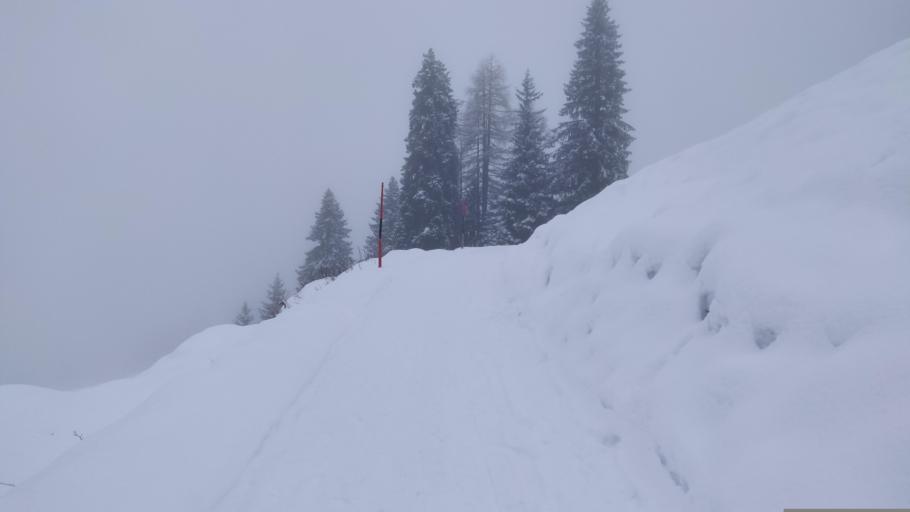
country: CH
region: Bern
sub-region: Interlaken-Oberhasli District
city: Lauterbrunnen
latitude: 46.5907
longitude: 7.8927
